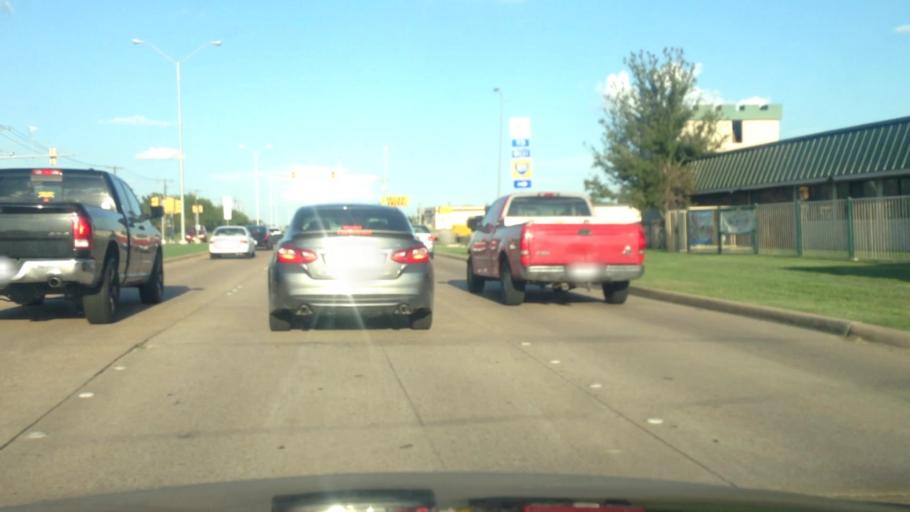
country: US
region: Texas
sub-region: Tarrant County
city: Watauga
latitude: 32.8609
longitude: -97.2814
